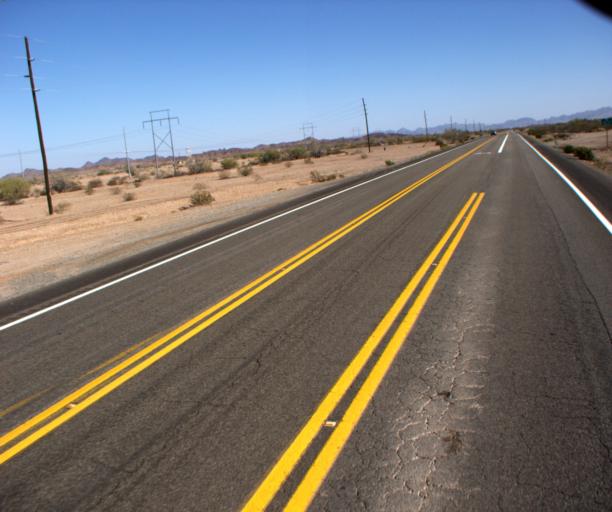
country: US
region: Arizona
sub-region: Yuma County
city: Fortuna Foothills
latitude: 32.9157
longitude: -114.3232
